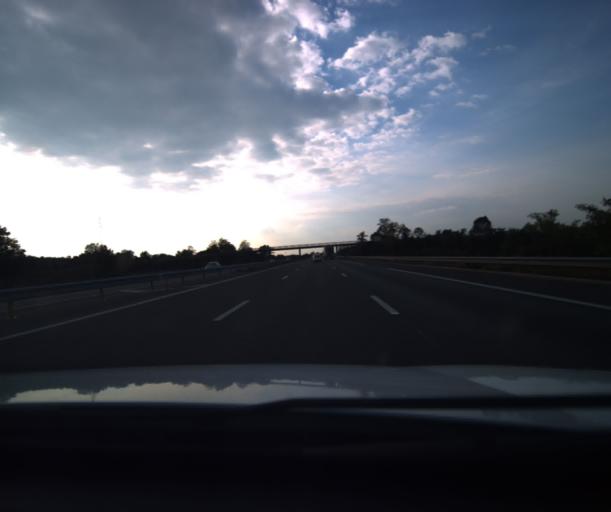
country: FR
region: Midi-Pyrenees
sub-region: Departement du Tarn-et-Garonne
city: Pompignan
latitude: 43.8382
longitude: 1.3329
